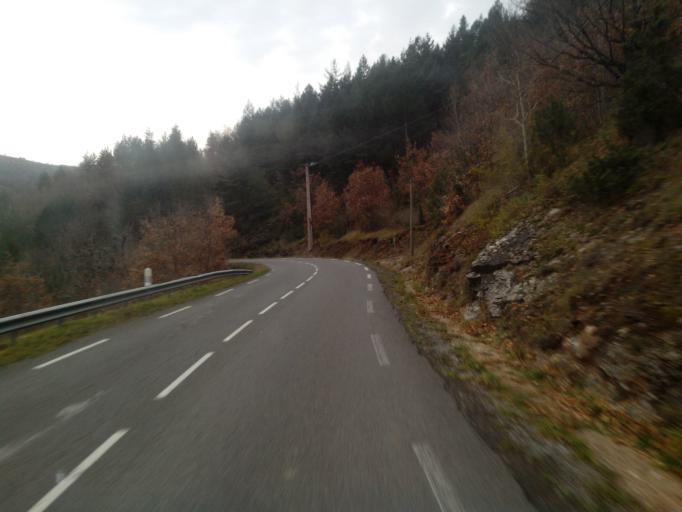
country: FR
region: Languedoc-Roussillon
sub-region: Departement de la Lozere
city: Florac
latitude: 44.2933
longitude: 3.5963
